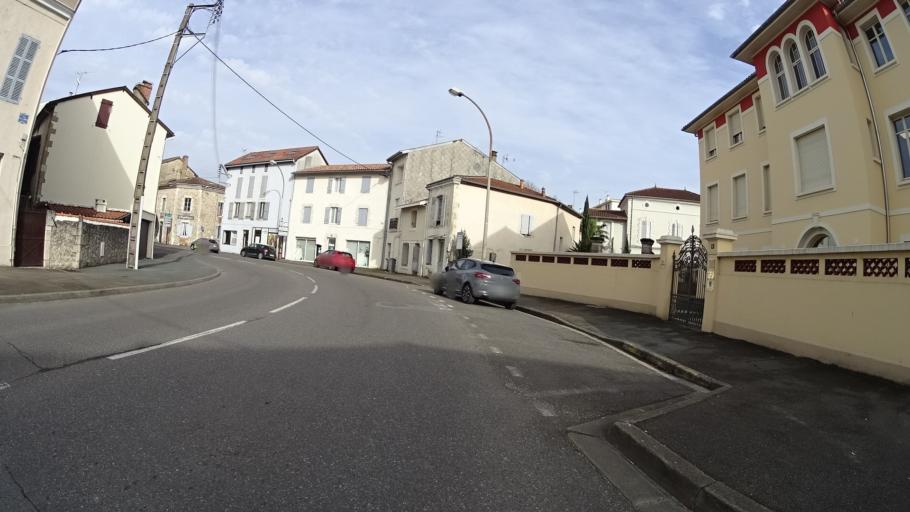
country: FR
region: Aquitaine
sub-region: Departement des Landes
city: Dax
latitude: 43.7076
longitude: -1.0505
